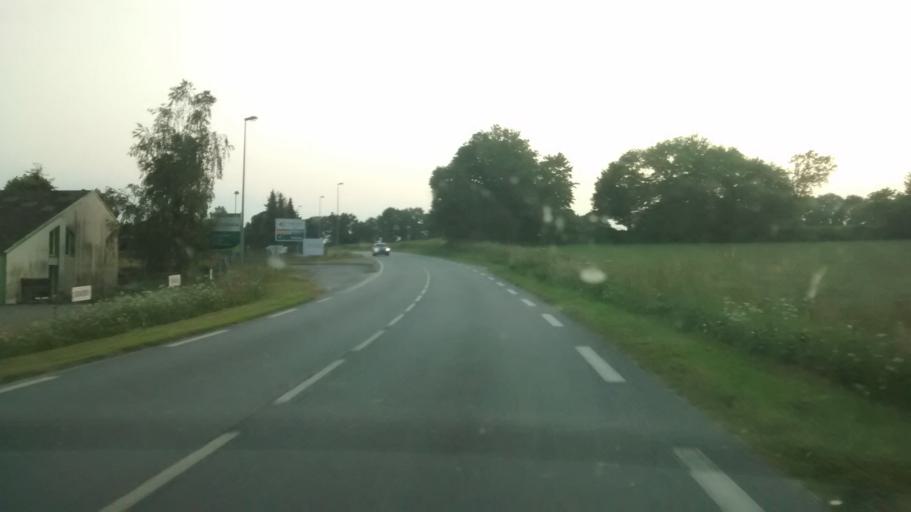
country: FR
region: Brittany
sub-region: Departement du Morbihan
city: Guer
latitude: 47.9117
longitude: -2.1280
